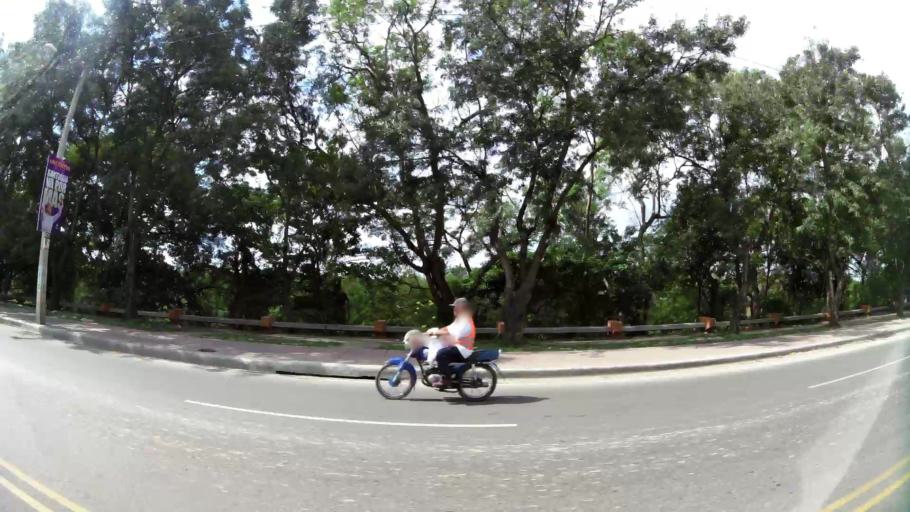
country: DO
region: Santiago
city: Santiago de los Caballeros
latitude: 19.4720
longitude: -70.7189
